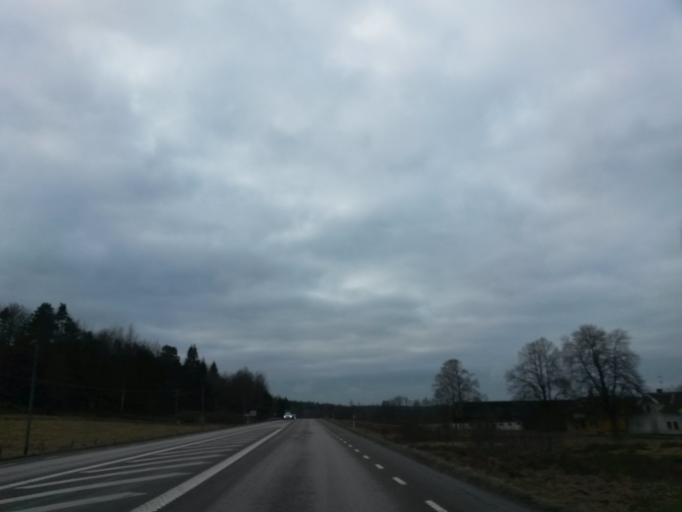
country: SE
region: Vaestra Goetaland
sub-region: Alingsas Kommun
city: Alingsas
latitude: 57.9420
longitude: 12.5900
